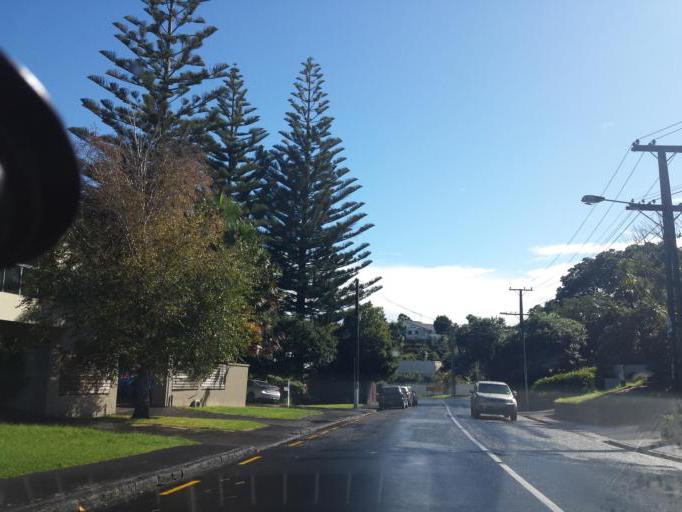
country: NZ
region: Auckland
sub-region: Auckland
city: Tamaki
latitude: -36.8512
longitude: 174.8630
